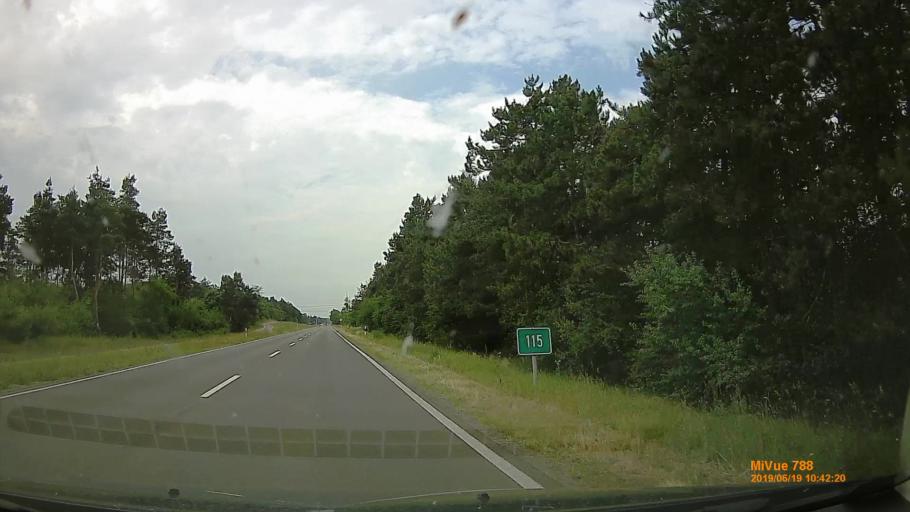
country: HU
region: Tolna
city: Paks
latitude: 46.5786
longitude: 18.8371
